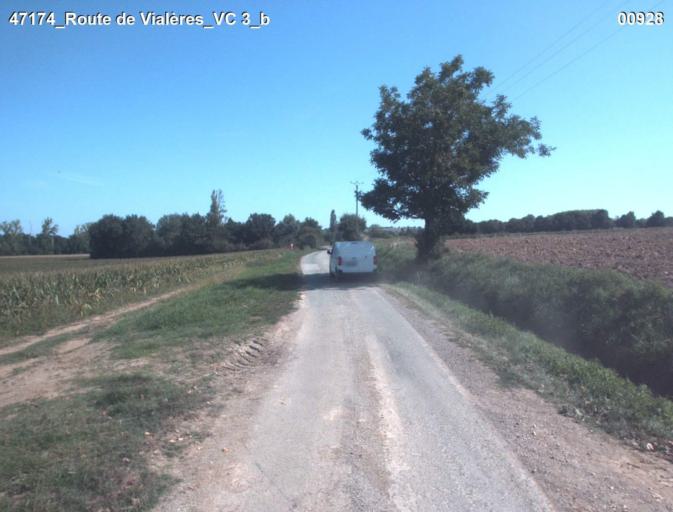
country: FR
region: Midi-Pyrenees
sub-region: Departement du Gers
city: Condom
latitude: 44.0426
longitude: 0.3756
